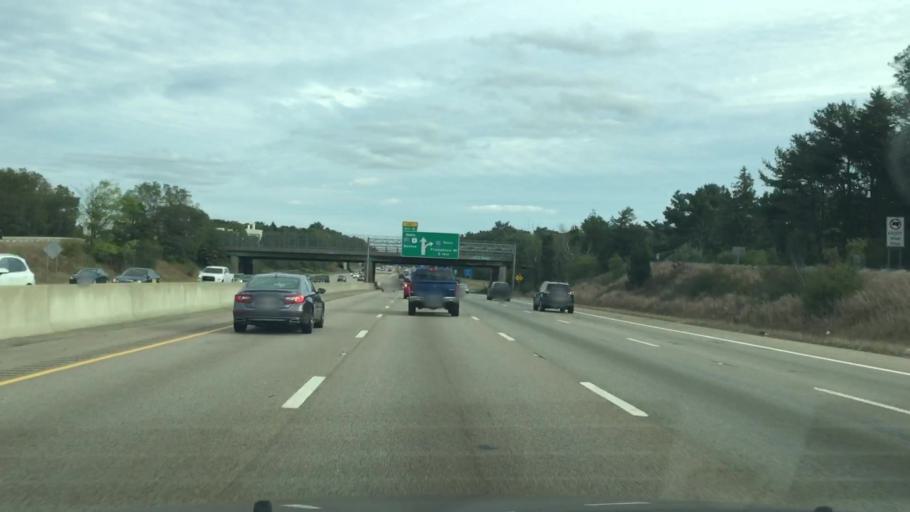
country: US
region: Massachusetts
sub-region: Norfolk County
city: Dedham
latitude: 42.2243
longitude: -71.1740
